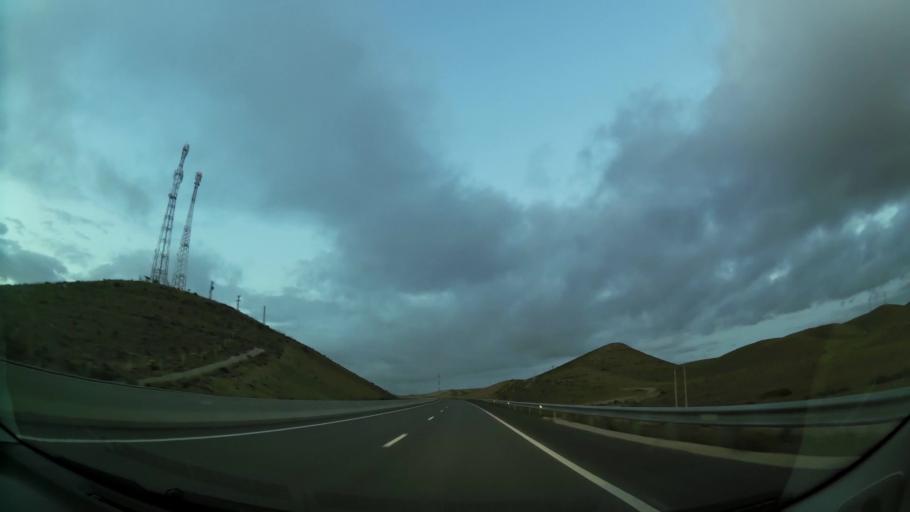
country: MA
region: Oriental
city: El Aioun
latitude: 34.6150
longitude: -2.4161
